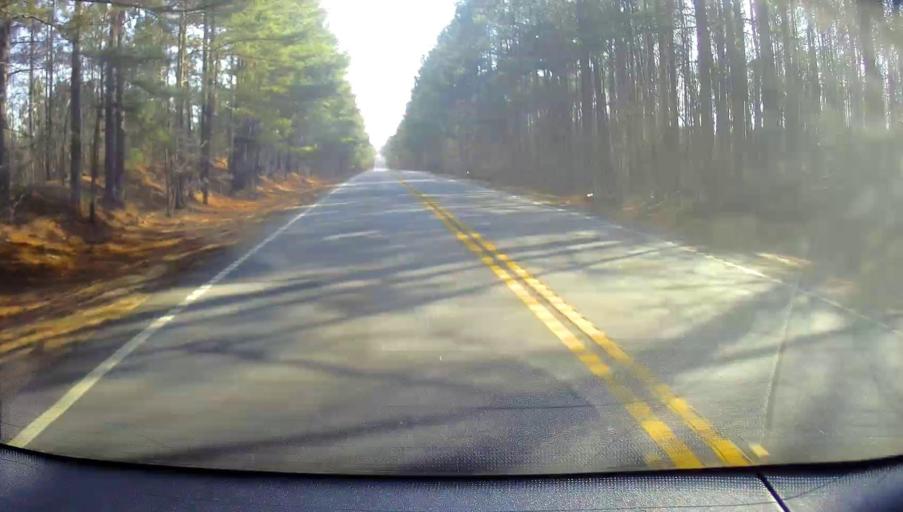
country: US
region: Georgia
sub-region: Butts County
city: Indian Springs
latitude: 33.1569
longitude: -83.8398
